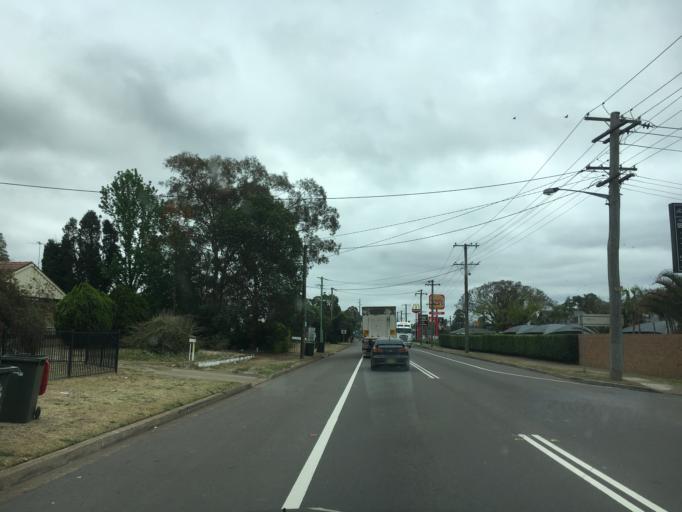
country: AU
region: New South Wales
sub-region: Singleton
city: Singleton
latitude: -32.5708
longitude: 151.1811
